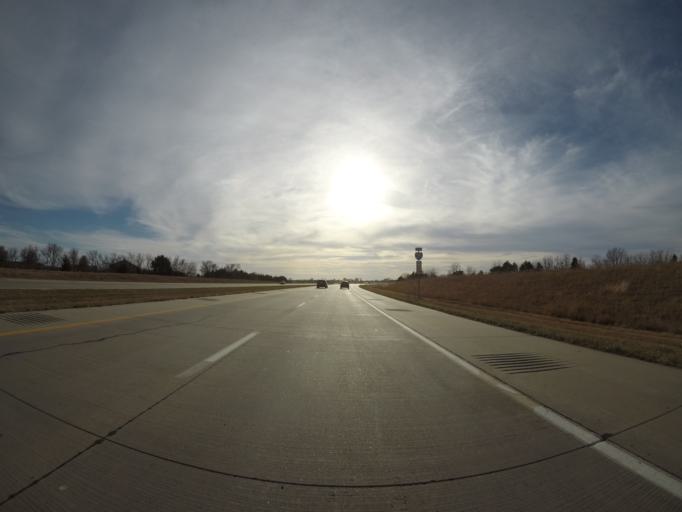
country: US
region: Kansas
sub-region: Franklin County
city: Ottawa
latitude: 38.5880
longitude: -95.2379
